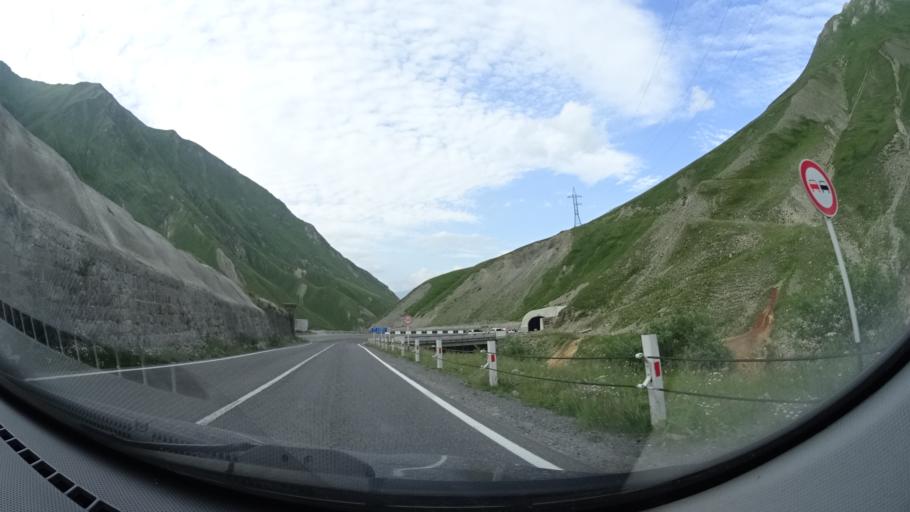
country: GE
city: Gudauri
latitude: 42.5339
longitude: 44.4744
